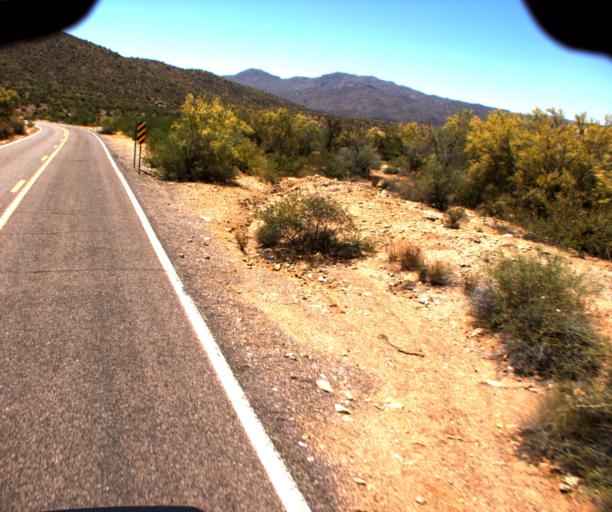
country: US
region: Arizona
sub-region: Yavapai County
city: Bagdad
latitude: 34.4607
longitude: -113.0302
